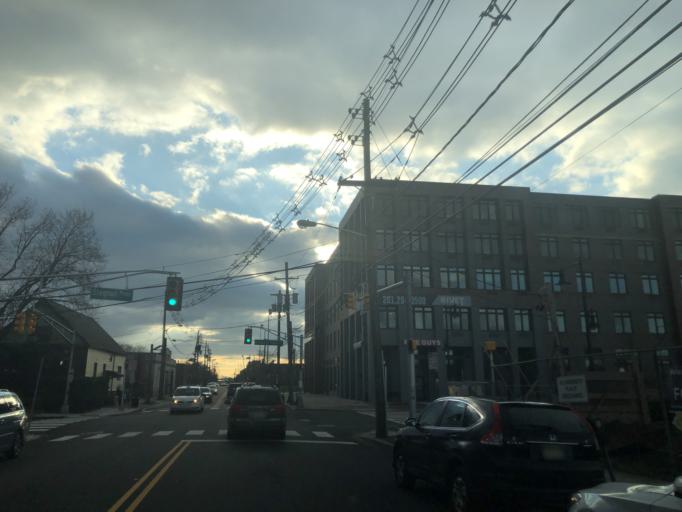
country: US
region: New Jersey
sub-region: Hudson County
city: Jersey City
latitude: 40.7114
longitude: -74.0930
